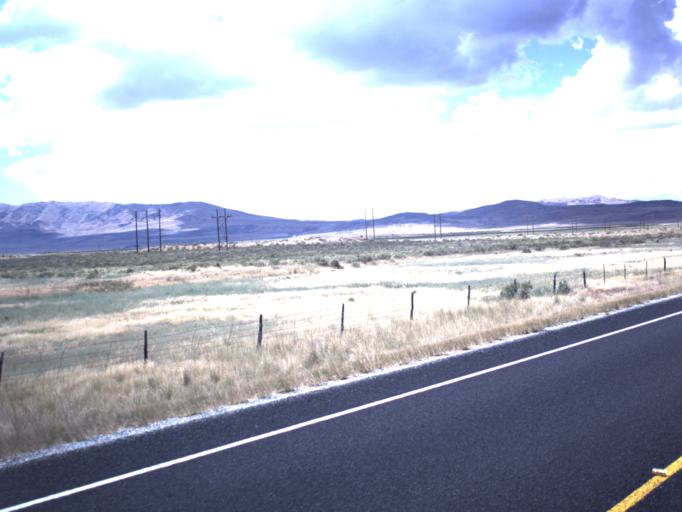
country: US
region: Utah
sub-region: Box Elder County
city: Tremonton
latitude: 41.6201
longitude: -112.3859
